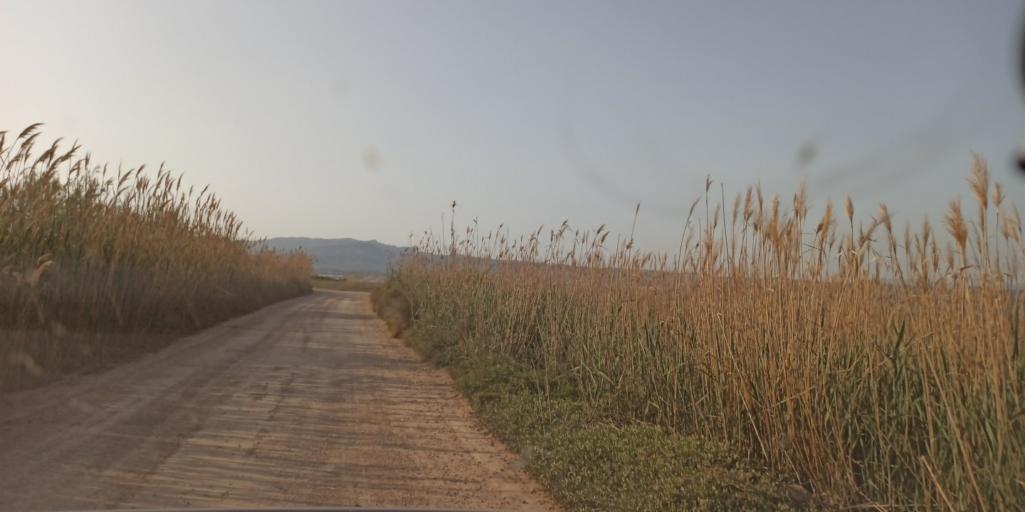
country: ES
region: Catalonia
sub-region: Provincia de Tarragona
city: L'Ampolla
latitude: 40.7766
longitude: 0.7231
